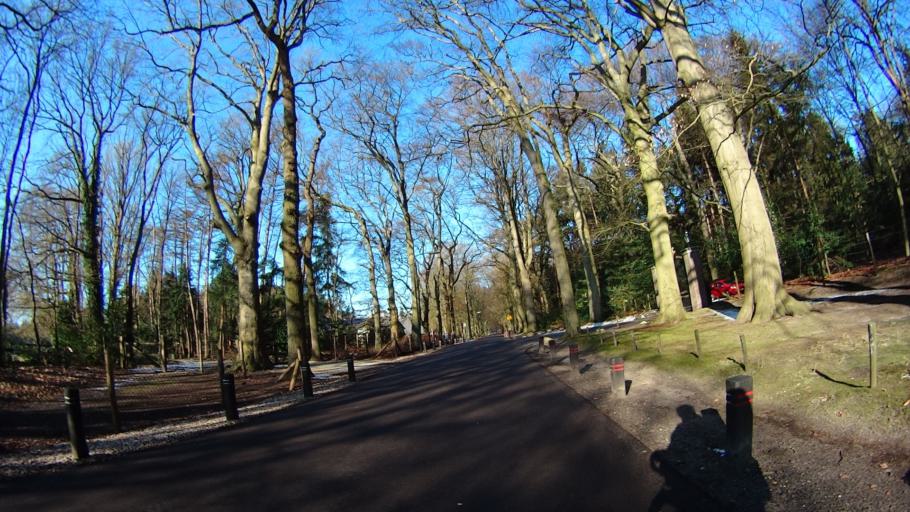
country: NL
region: North Holland
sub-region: Gemeente Hilversum
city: Hilversum
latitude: 52.1820
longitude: 5.2219
